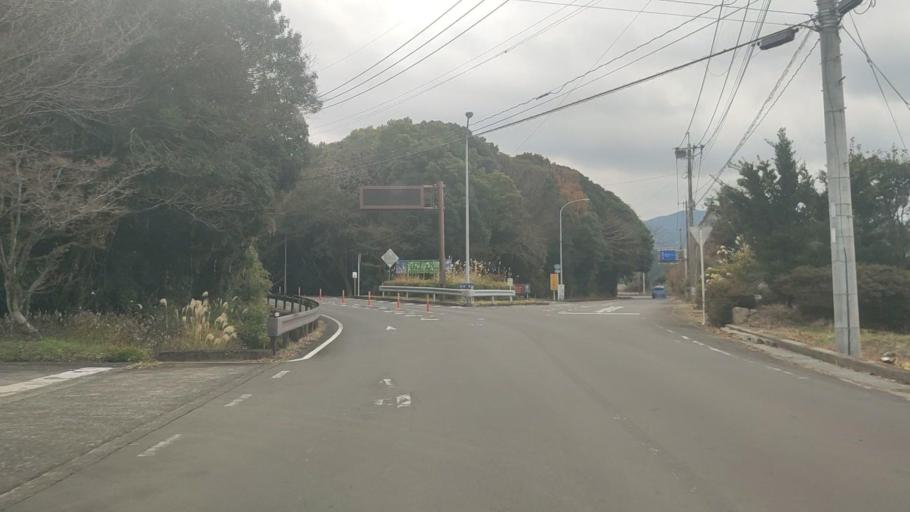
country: JP
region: Nagasaki
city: Shimabara
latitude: 32.8246
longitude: 130.2916
